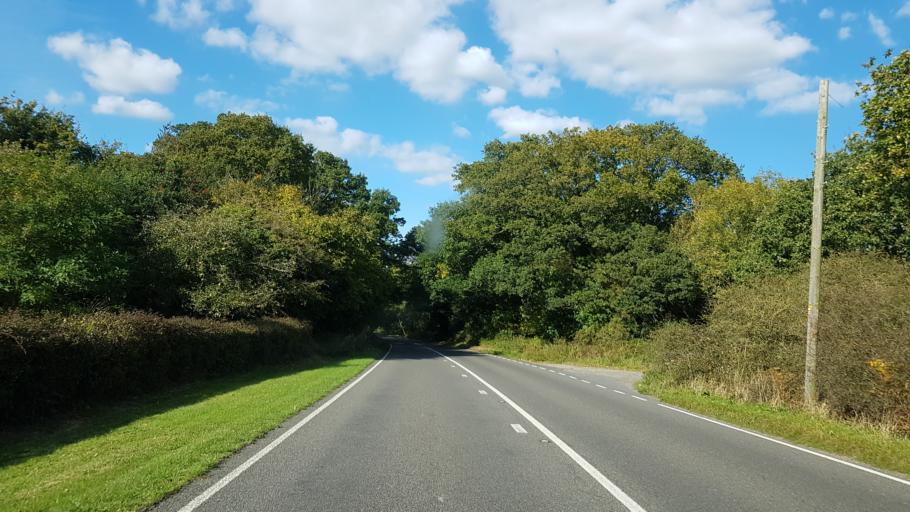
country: GB
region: England
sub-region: West Sussex
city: Petworth
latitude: 51.0230
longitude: -0.6239
